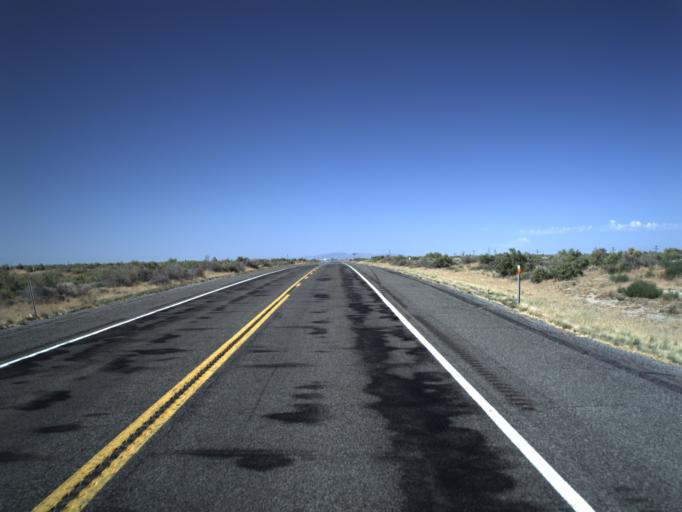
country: US
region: Utah
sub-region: Millard County
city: Delta
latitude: 39.4181
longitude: -112.4797
